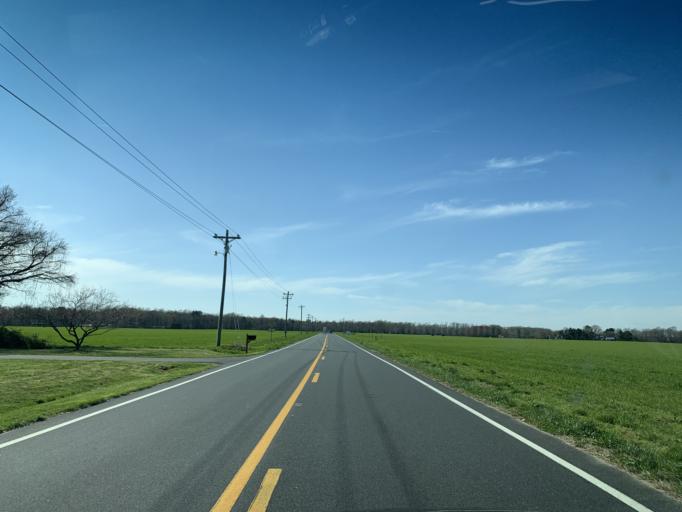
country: US
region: Delaware
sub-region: Sussex County
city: Milford
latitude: 38.9490
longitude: -75.4683
